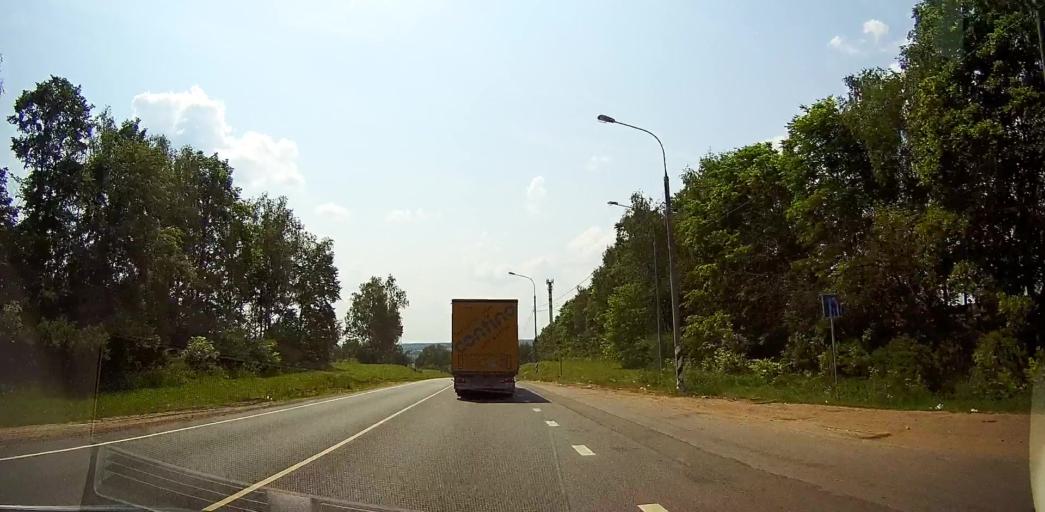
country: RU
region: Moskovskaya
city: Meshcherino
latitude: 55.1988
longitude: 38.3713
